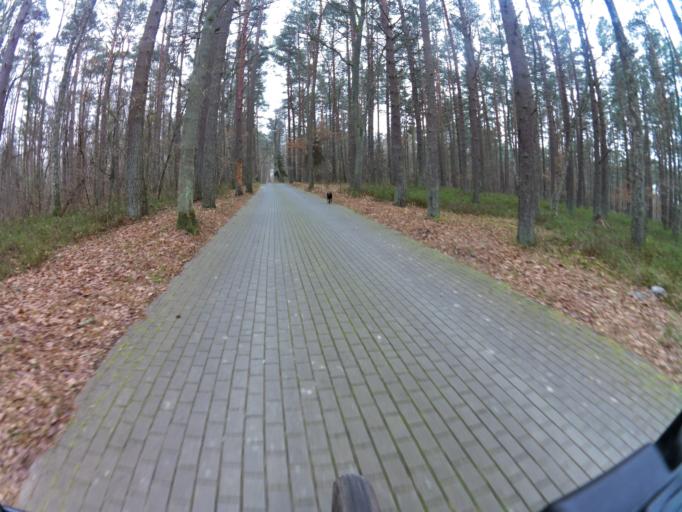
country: PL
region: West Pomeranian Voivodeship
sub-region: Powiat gryficki
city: Cerkwica
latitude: 54.0970
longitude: 15.1290
